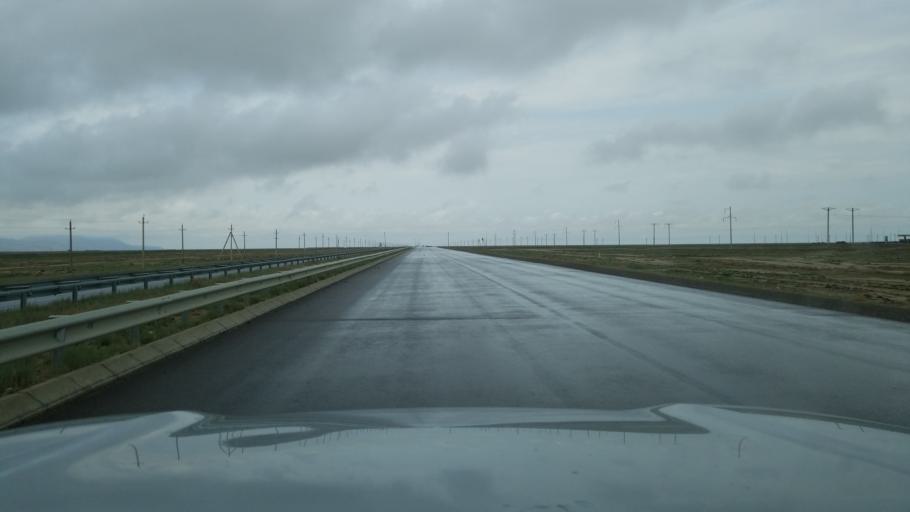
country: TM
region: Balkan
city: Gazanjyk
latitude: 39.1452
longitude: 55.8646
